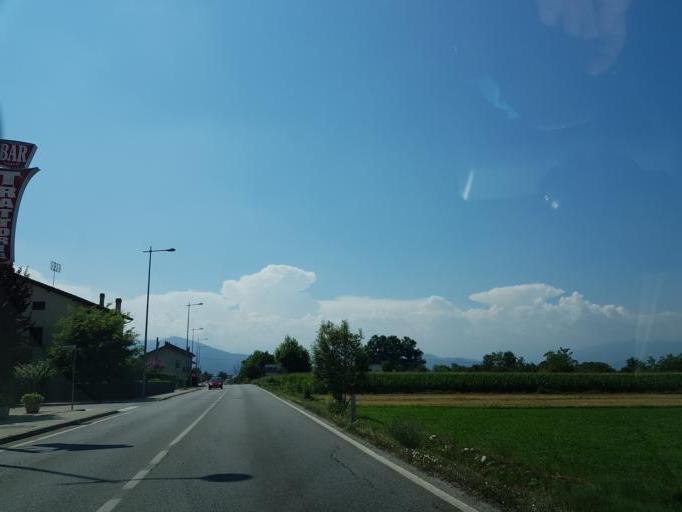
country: IT
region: Piedmont
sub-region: Provincia di Cuneo
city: San Defendente
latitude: 44.3950
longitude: 7.5070
